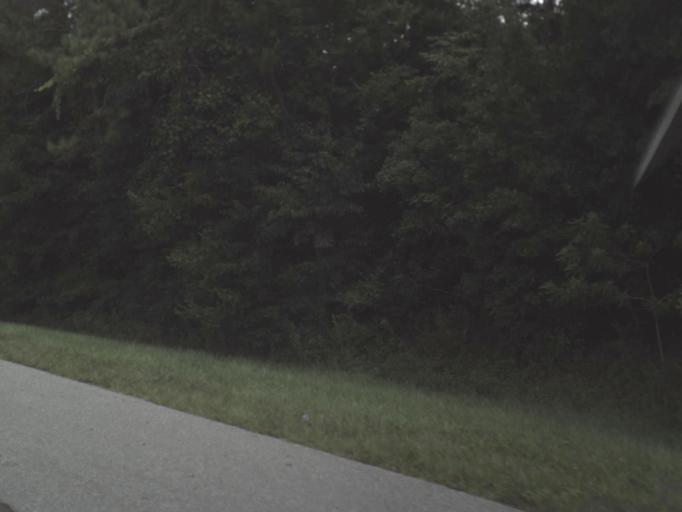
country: US
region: Florida
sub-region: Hernando County
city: Hill 'n Dale
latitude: 28.4733
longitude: -82.2605
